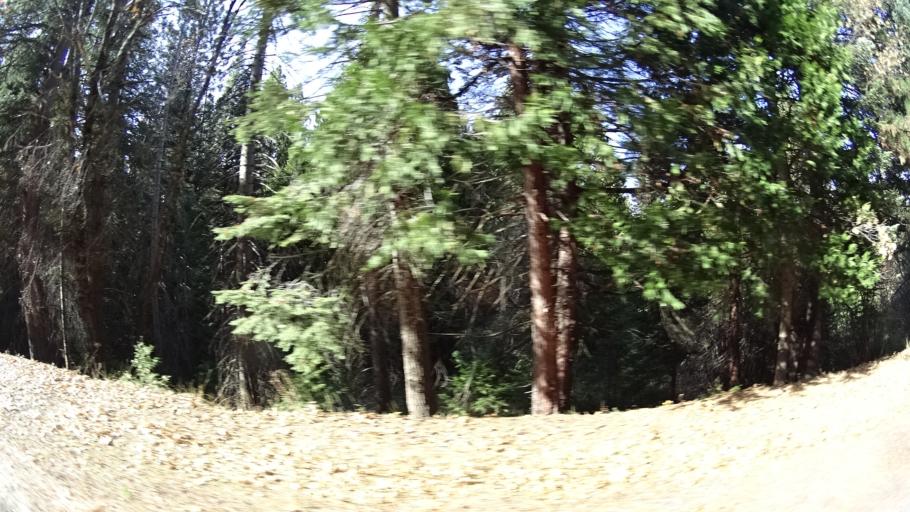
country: US
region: California
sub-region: Siskiyou County
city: Weed
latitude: 41.4079
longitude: -122.4002
